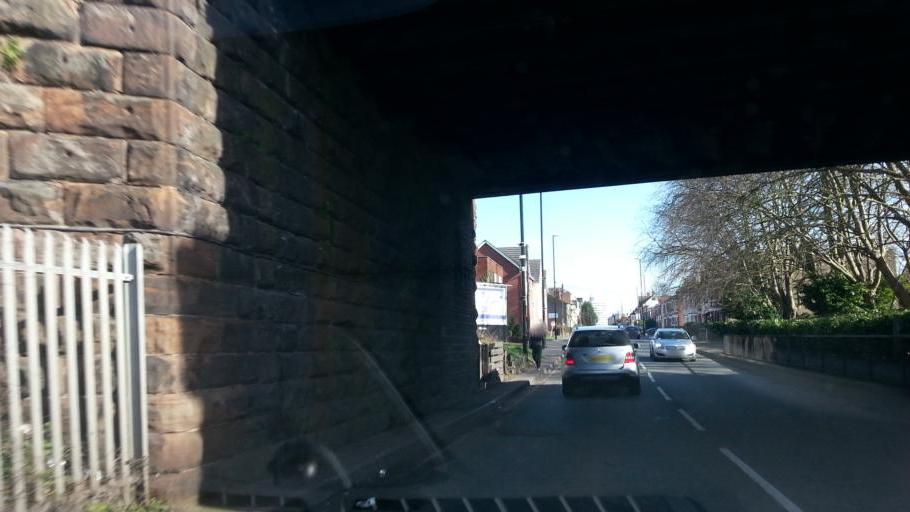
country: GB
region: England
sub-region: Coventry
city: Coventry
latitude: 52.4120
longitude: -1.5258
